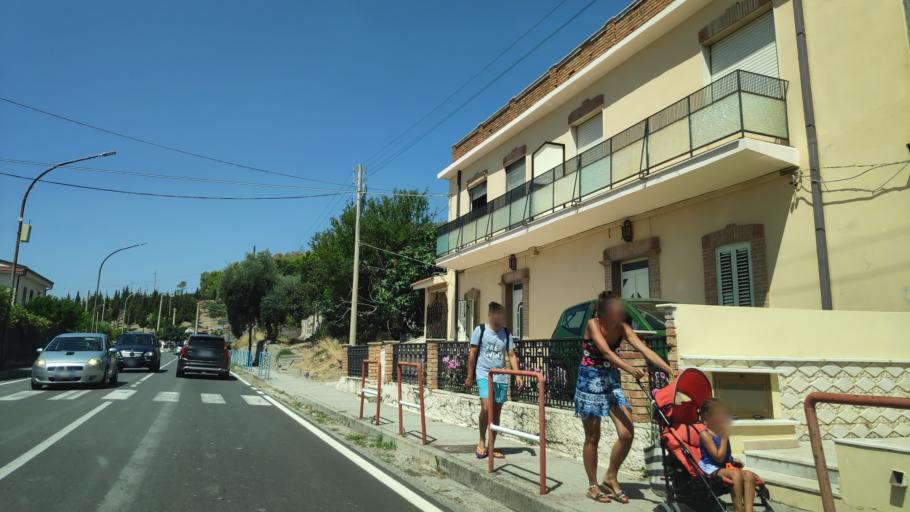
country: IT
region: Calabria
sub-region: Provincia di Reggio Calabria
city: Palizzi Marina
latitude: 37.9248
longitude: 16.0373
